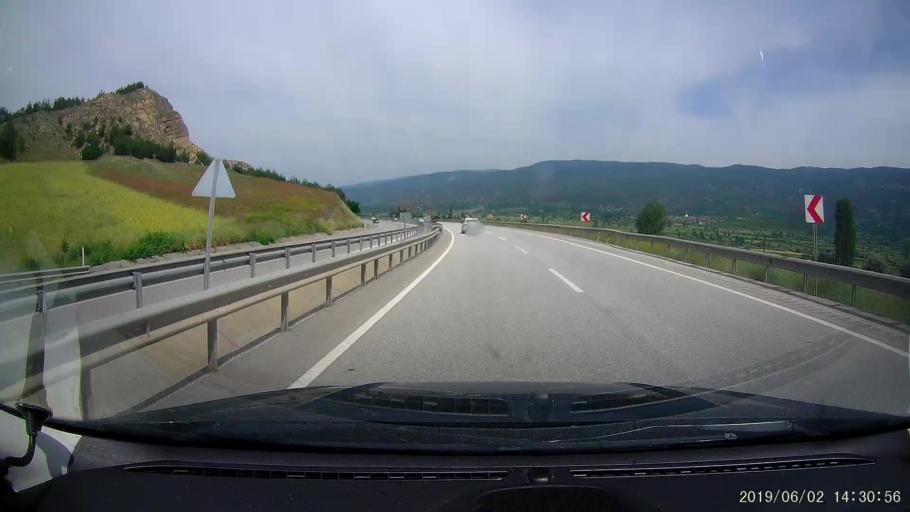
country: TR
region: Kastamonu
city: Tosya
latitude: 41.0147
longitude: 34.1268
